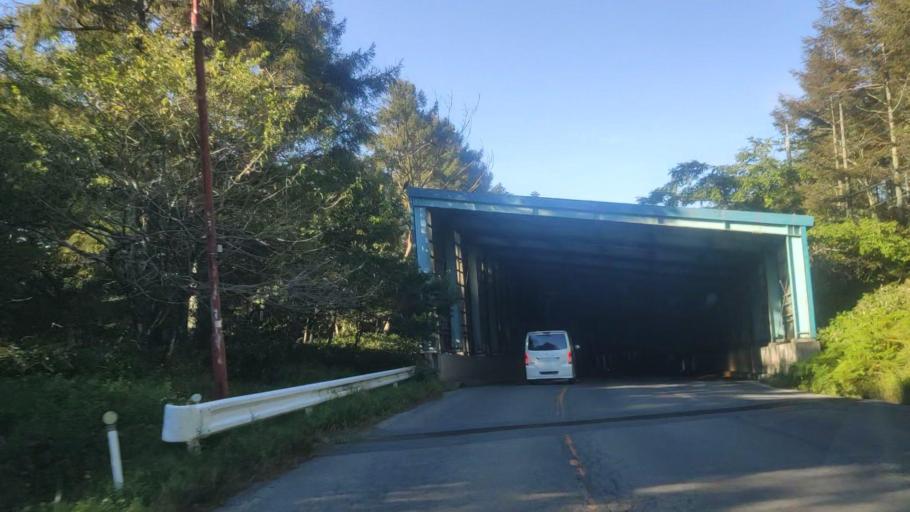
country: JP
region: Nagano
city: Kamimaruko
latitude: 36.1767
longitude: 138.2815
